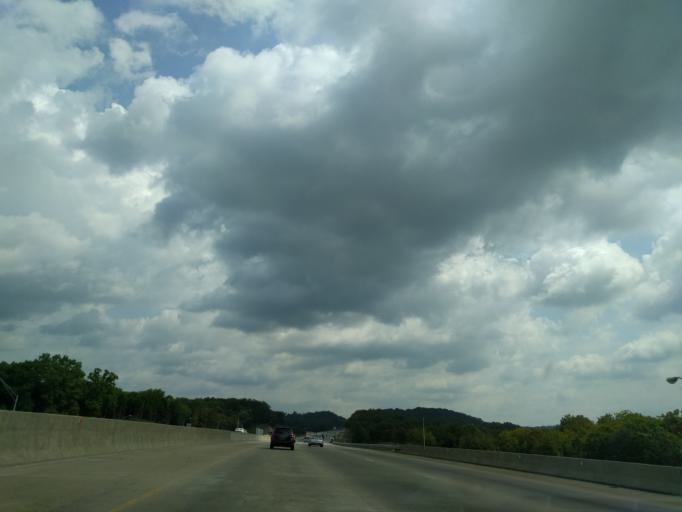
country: US
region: Kentucky
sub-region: Barren County
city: Cave City
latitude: 37.0976
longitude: -86.0548
